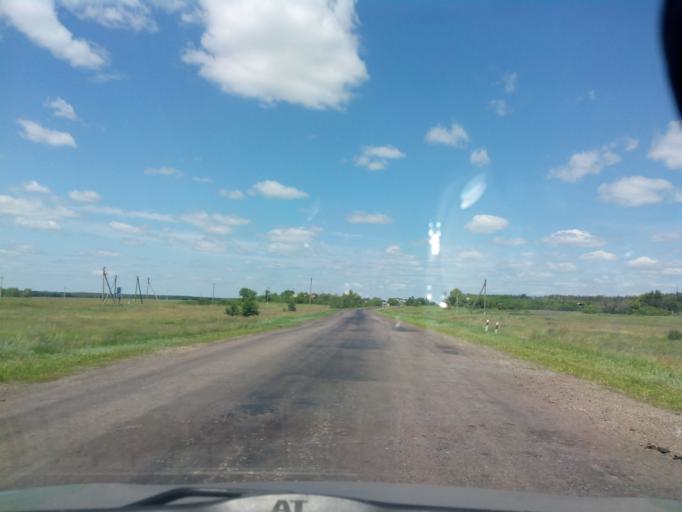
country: RU
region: Voronezj
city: Ternovka
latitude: 51.7277
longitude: 41.5176
